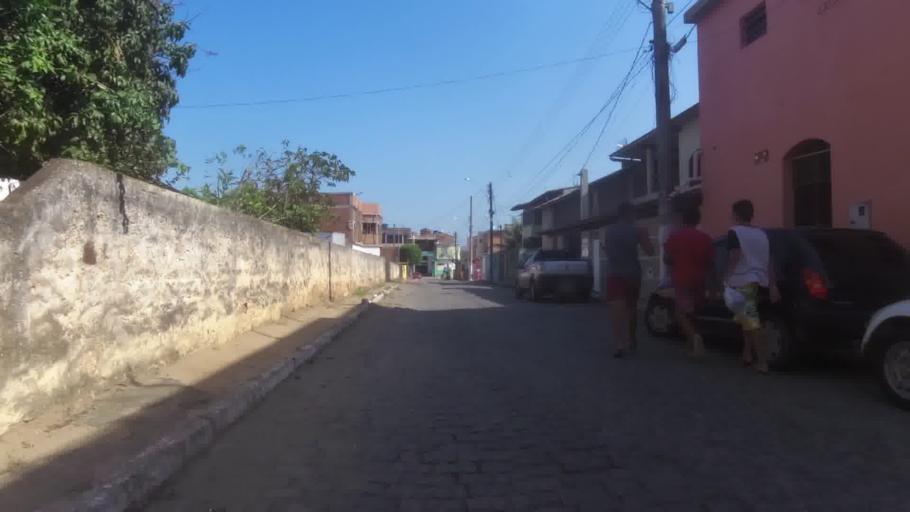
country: BR
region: Espirito Santo
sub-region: Itapemirim
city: Itapemirim
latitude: -21.0099
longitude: -40.8132
